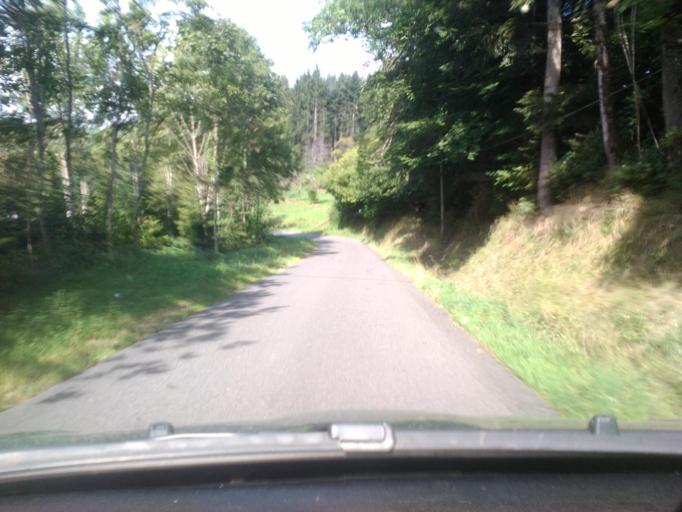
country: FR
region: Lorraine
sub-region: Departement des Vosges
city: Fraize
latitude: 48.2128
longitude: 7.0180
